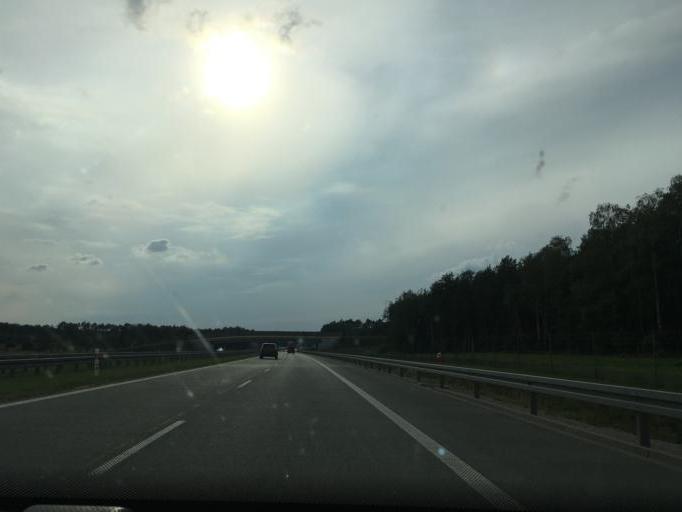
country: PL
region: Lodz Voivodeship
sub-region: Powiat pabianicki
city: Dobron
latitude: 51.6044
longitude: 19.2936
